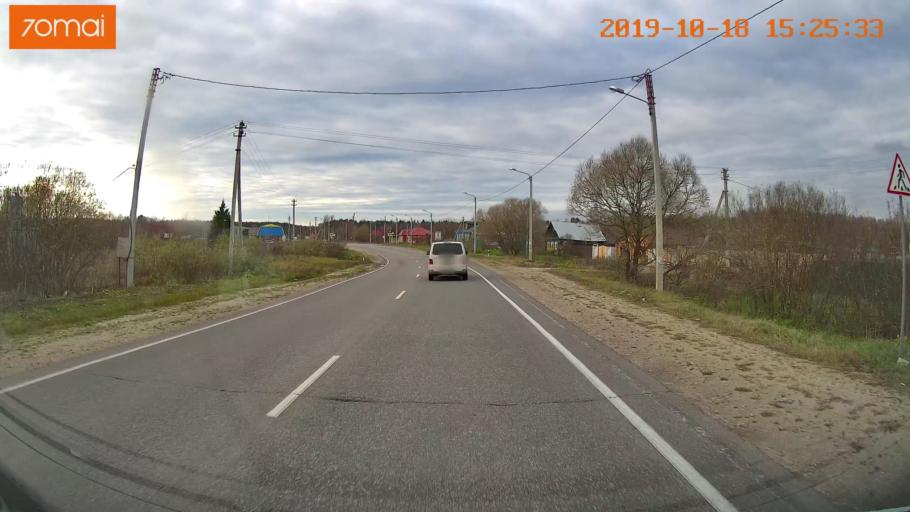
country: RU
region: Vladimir
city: Anopino
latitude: 55.7418
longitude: 40.7040
